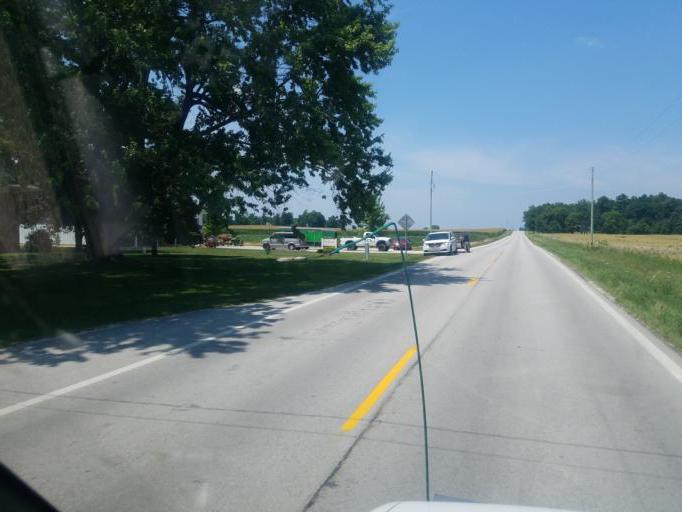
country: US
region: Ohio
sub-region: Auglaize County
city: Minster
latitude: 40.4095
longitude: -84.4338
